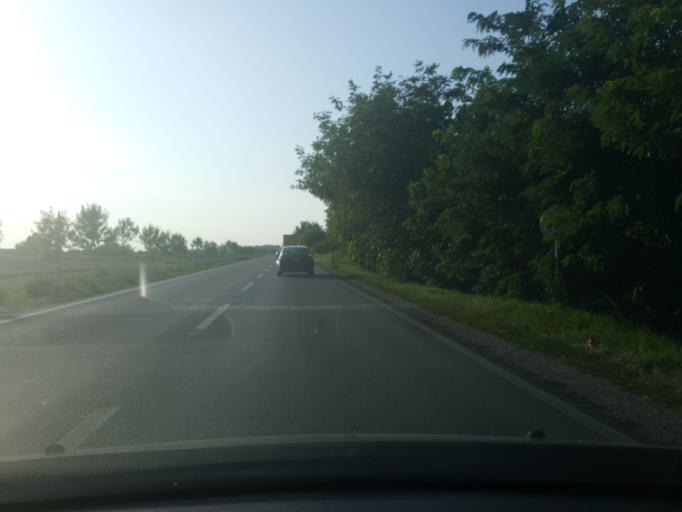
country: RS
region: Central Serbia
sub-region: Macvanski Okrug
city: Sabac
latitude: 44.7416
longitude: 19.6737
